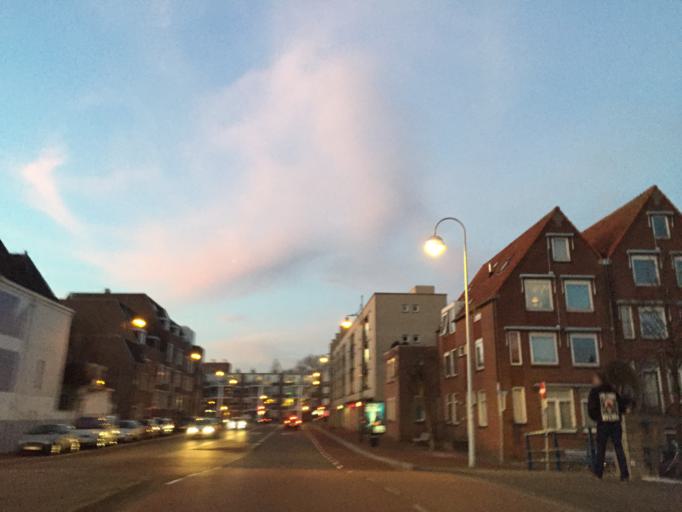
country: NL
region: South Holland
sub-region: Gemeente Leiden
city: Leiden
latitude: 52.1618
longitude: 4.4976
